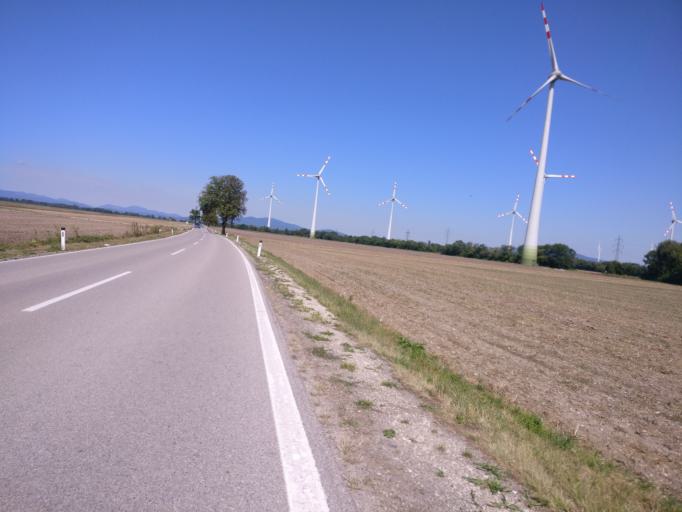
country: AT
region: Lower Austria
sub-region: Politischer Bezirk Baden
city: Pottendorf
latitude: 47.9242
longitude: 16.3656
